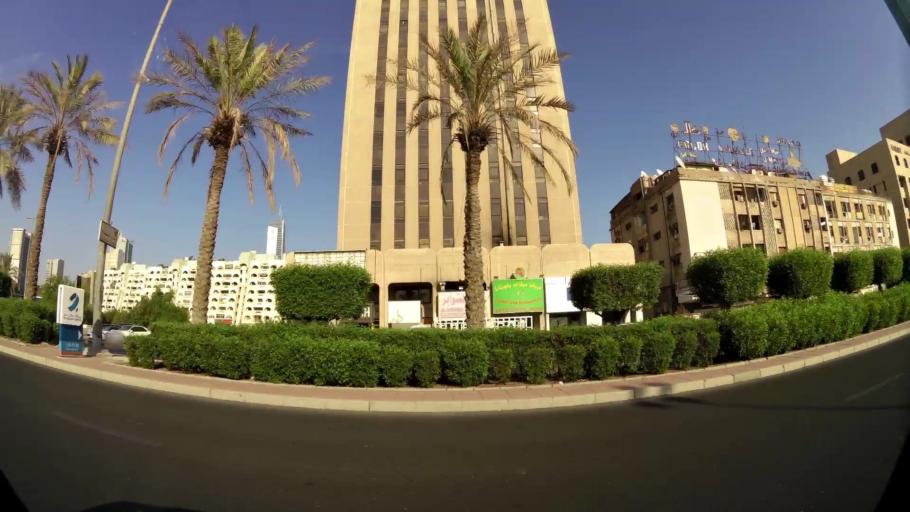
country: KW
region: Al Asimah
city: Kuwait City
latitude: 29.3749
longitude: 47.9828
